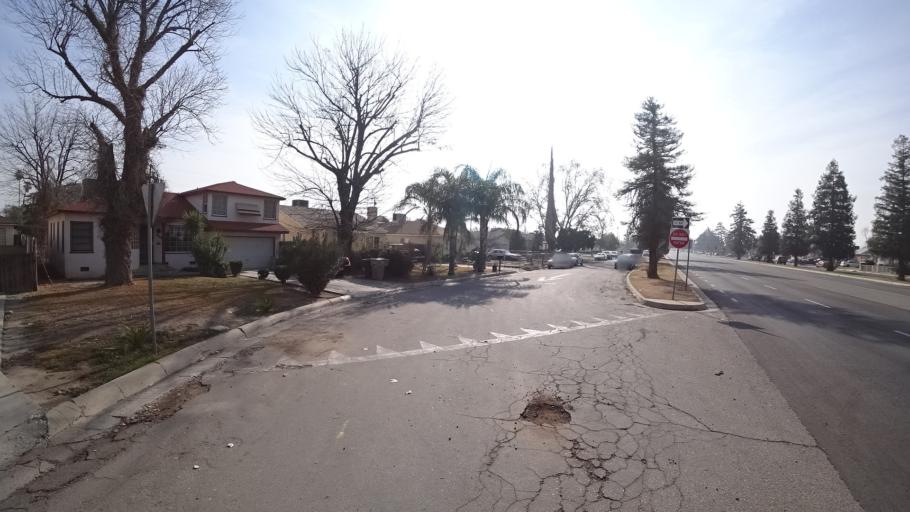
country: US
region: California
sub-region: Kern County
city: Bakersfield
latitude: 35.3483
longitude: -119.0188
